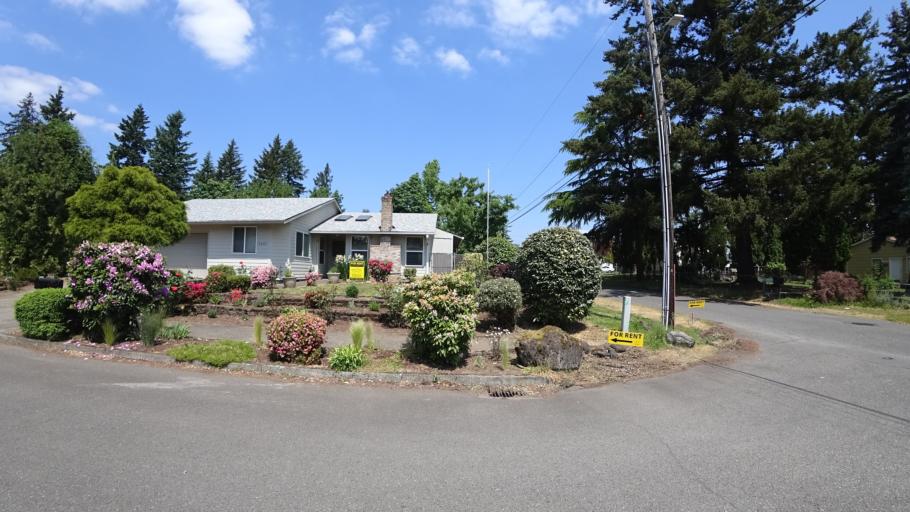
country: US
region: Oregon
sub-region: Multnomah County
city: Fairview
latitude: 45.5300
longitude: -122.4989
